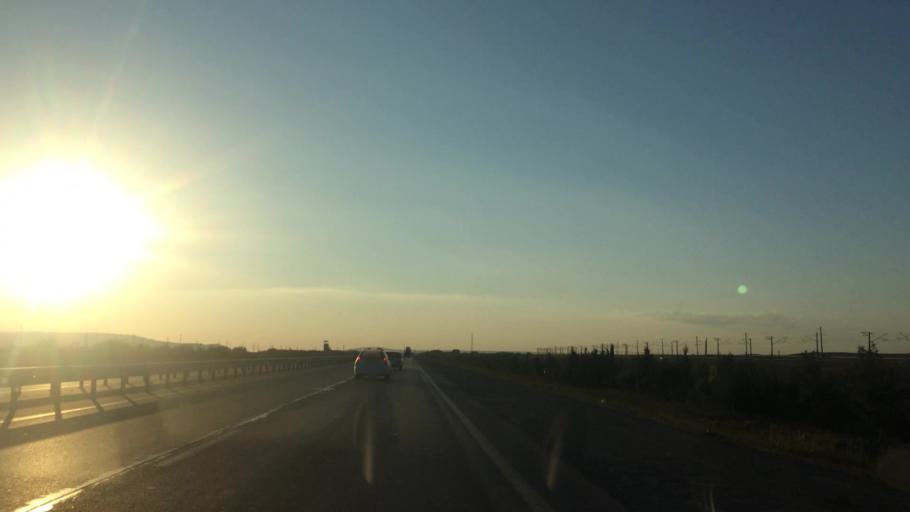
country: AZ
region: Baki
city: Qobustan
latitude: 39.9463
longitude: 49.3586
